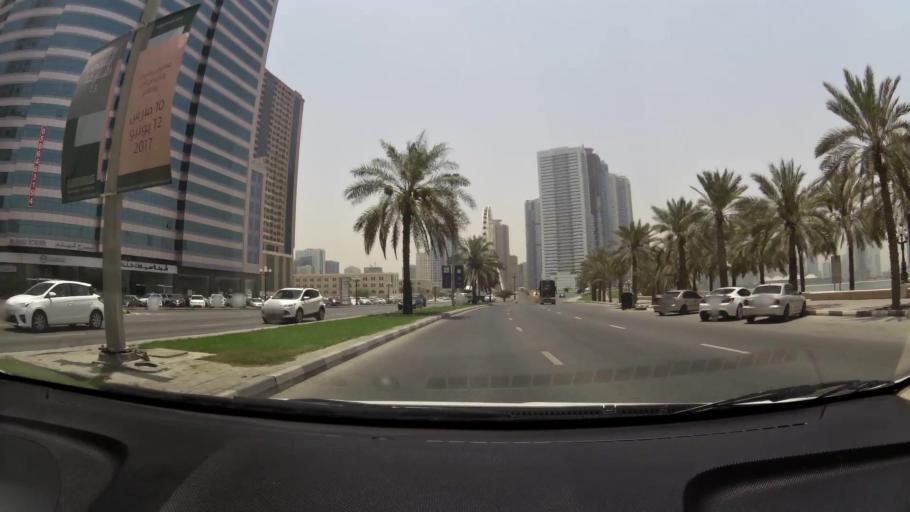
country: AE
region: Ash Shariqah
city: Sharjah
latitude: 25.3243
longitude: 55.3738
